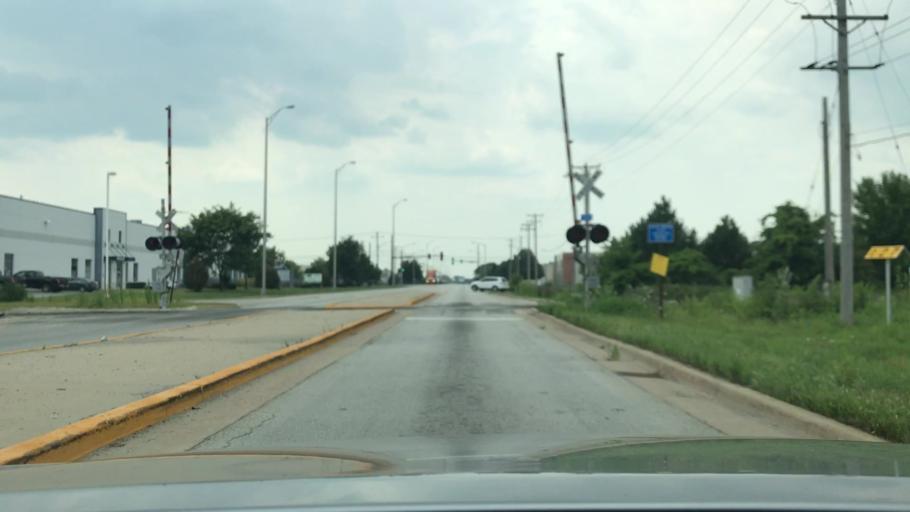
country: US
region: Illinois
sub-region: Will County
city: Plainfield
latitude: 41.6226
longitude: -88.2097
